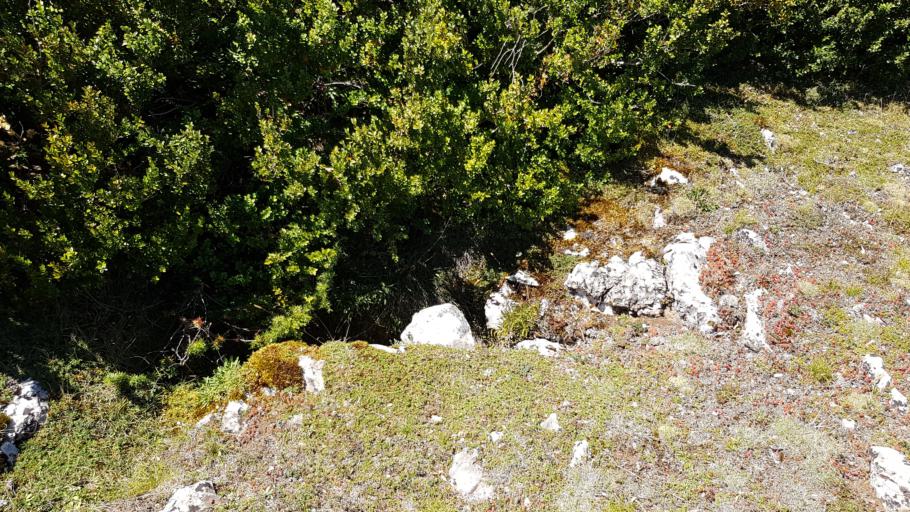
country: ES
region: La Rioja
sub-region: Provincia de La Rioja
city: Nestares
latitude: 42.2835
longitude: -2.6516
